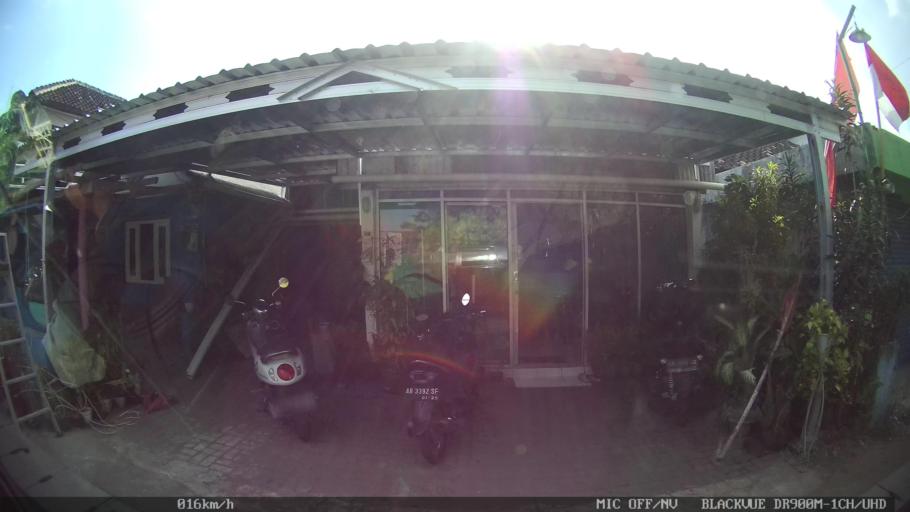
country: ID
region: Daerah Istimewa Yogyakarta
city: Gamping Lor
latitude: -7.7959
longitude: 110.3433
